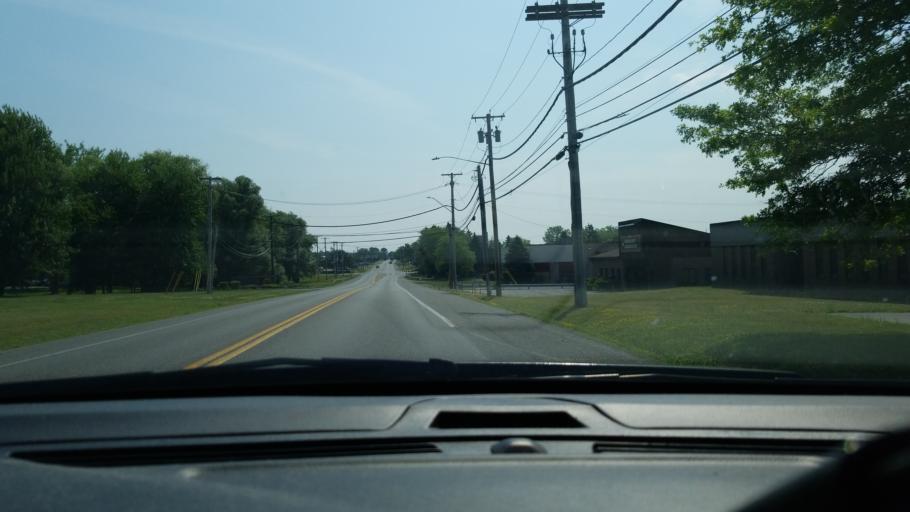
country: US
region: New York
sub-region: Onondaga County
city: Lyncourt
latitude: 43.0991
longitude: -76.0998
